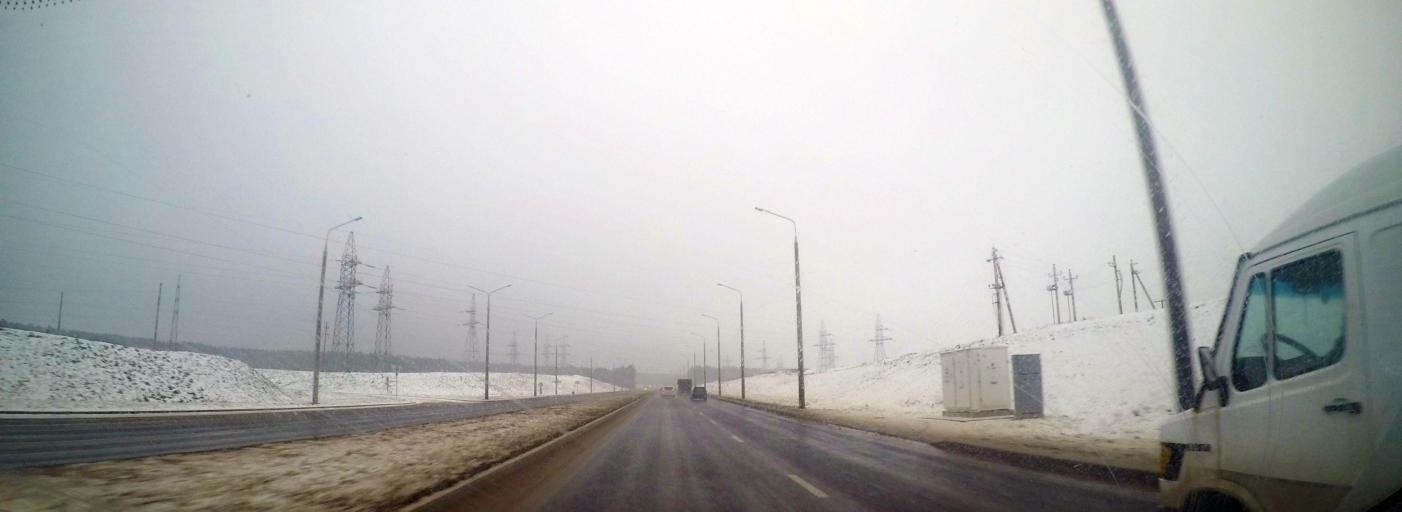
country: BY
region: Grodnenskaya
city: Hrodna
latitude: 53.6463
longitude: 23.8837
